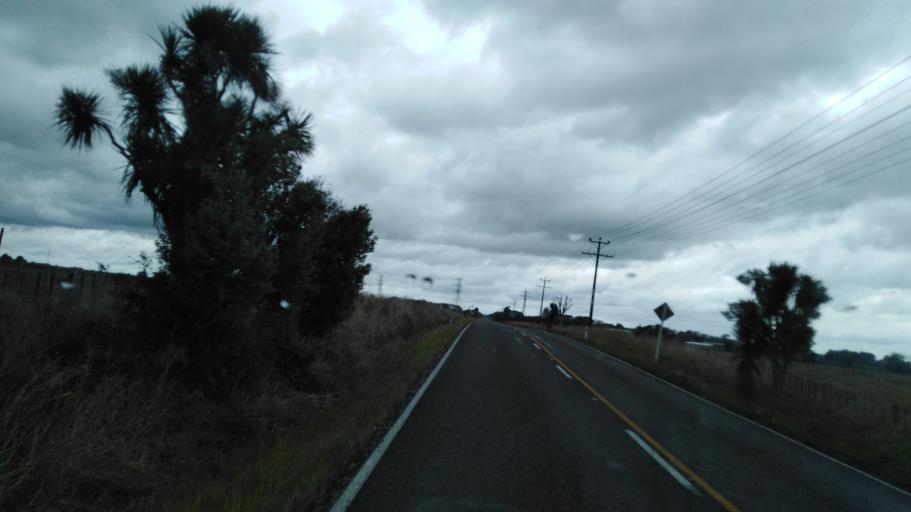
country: NZ
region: Manawatu-Wanganui
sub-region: Rangitikei District
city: Bulls
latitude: -40.1085
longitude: 175.3595
